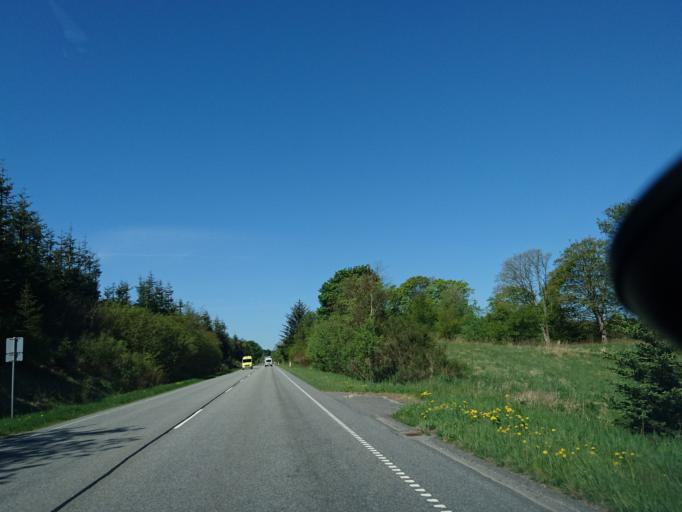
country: DK
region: North Denmark
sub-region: Hjorring Kommune
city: Sindal
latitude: 57.4579
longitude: 10.3340
